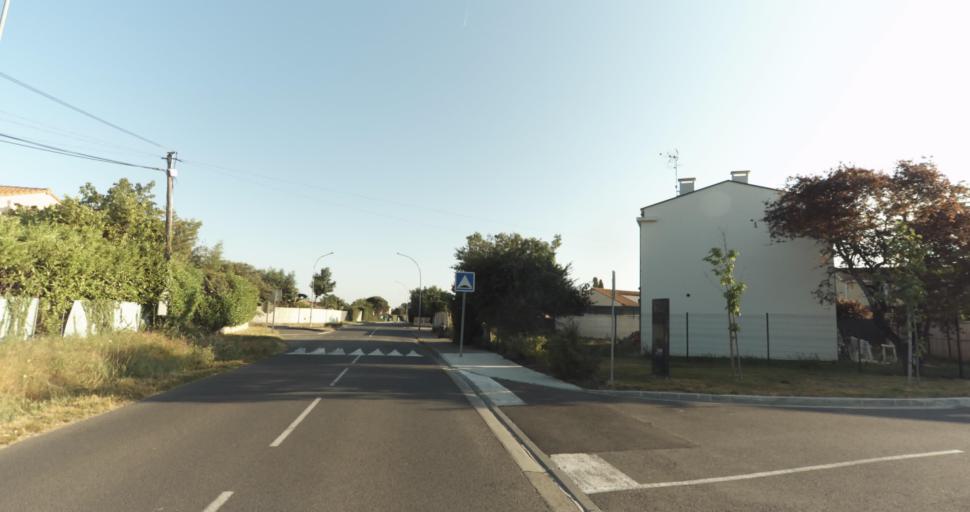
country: FR
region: Midi-Pyrenees
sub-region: Departement de la Haute-Garonne
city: Leguevin
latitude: 43.5924
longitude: 1.2358
